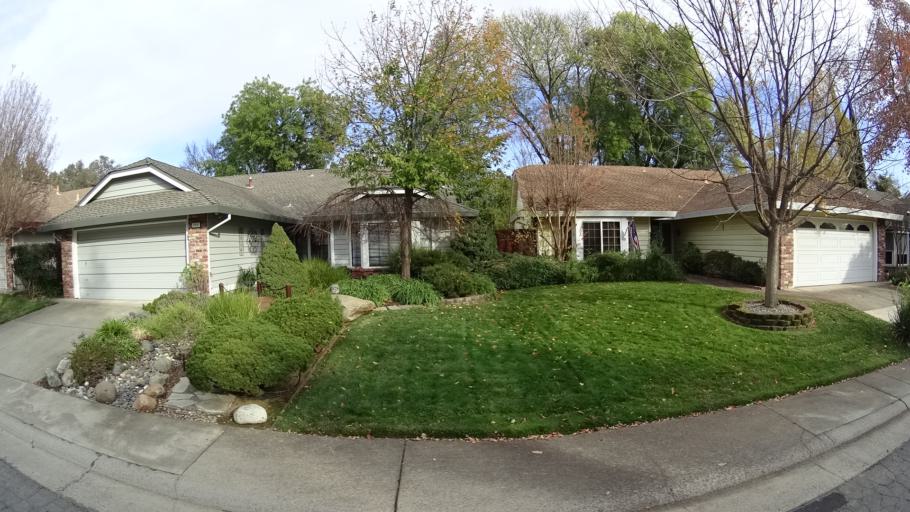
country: US
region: California
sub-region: Sacramento County
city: Citrus Heights
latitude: 38.7087
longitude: -121.2598
